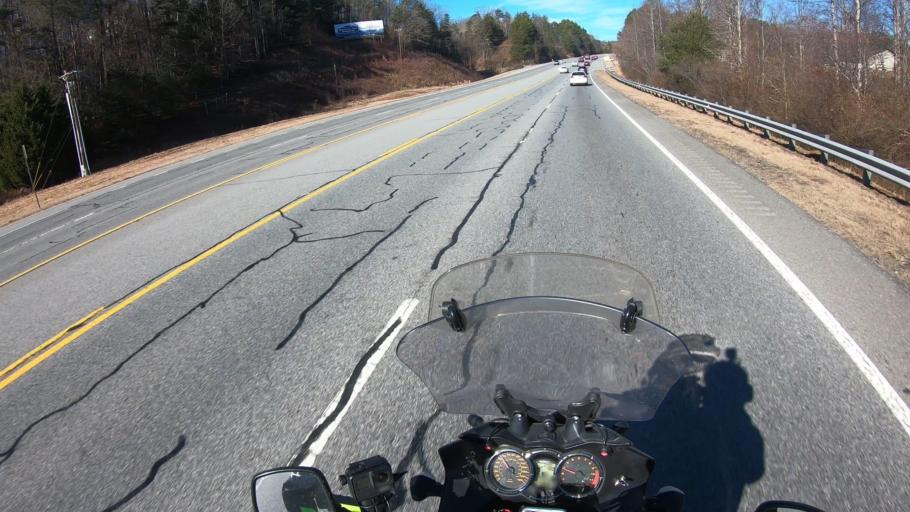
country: US
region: Georgia
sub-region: Fannin County
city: Blue Ridge
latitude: 34.8507
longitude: -84.3322
